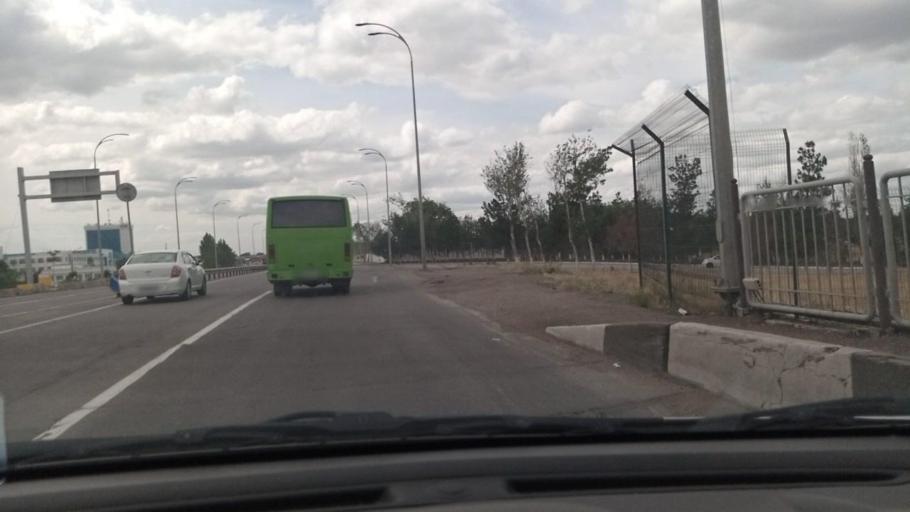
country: UZ
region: Toshkent Shahri
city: Bektemir
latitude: 41.2618
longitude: 69.3743
